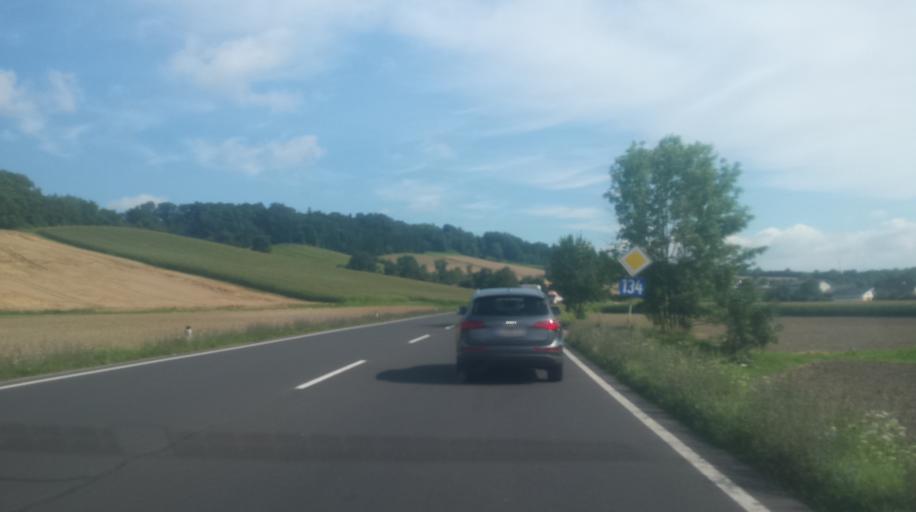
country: AT
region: Upper Austria
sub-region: Politischer Bezirk Grieskirchen
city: Bad Schallerbach
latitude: 48.2118
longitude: 13.9250
